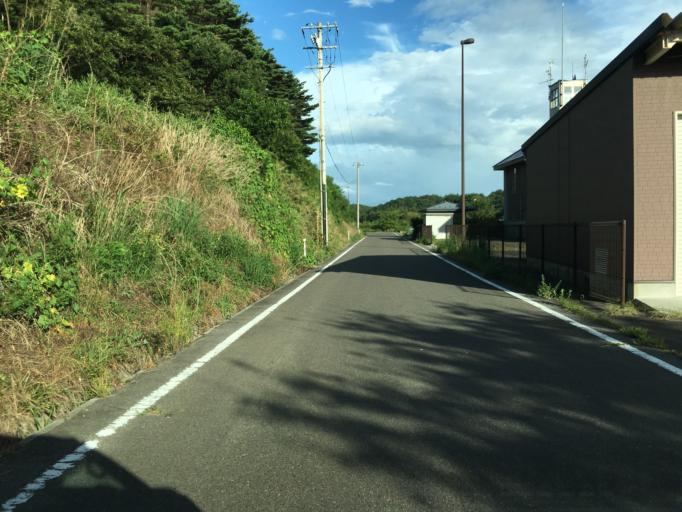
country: JP
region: Fukushima
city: Nihommatsu
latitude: 37.6322
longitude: 140.4177
